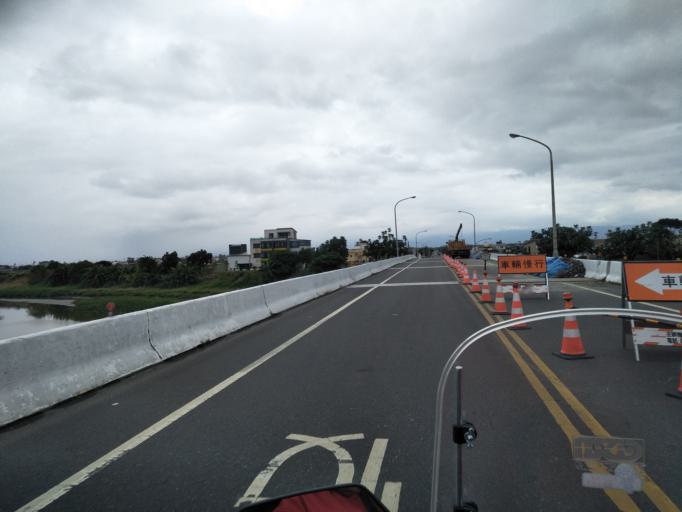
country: TW
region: Taiwan
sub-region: Yilan
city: Yilan
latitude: 24.8094
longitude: 121.7914
